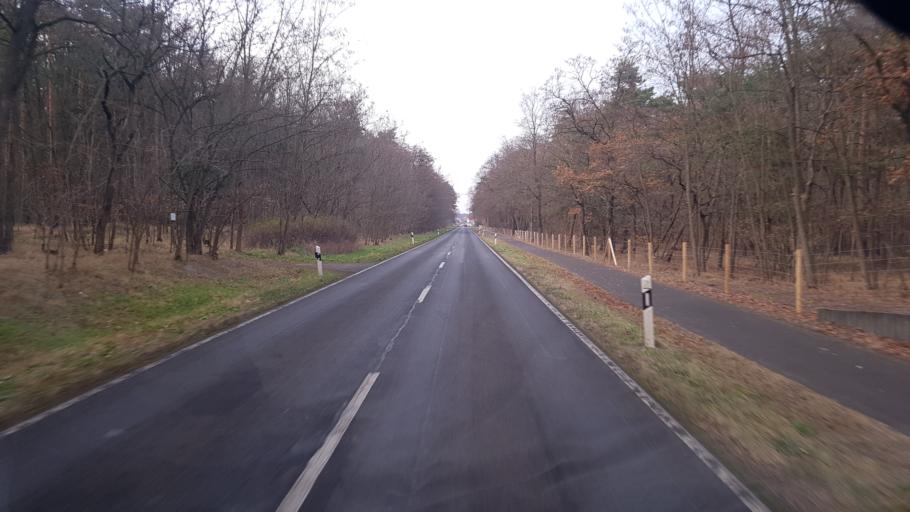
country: DE
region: Brandenburg
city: Ziltendorf
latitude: 52.1970
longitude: 14.6381
